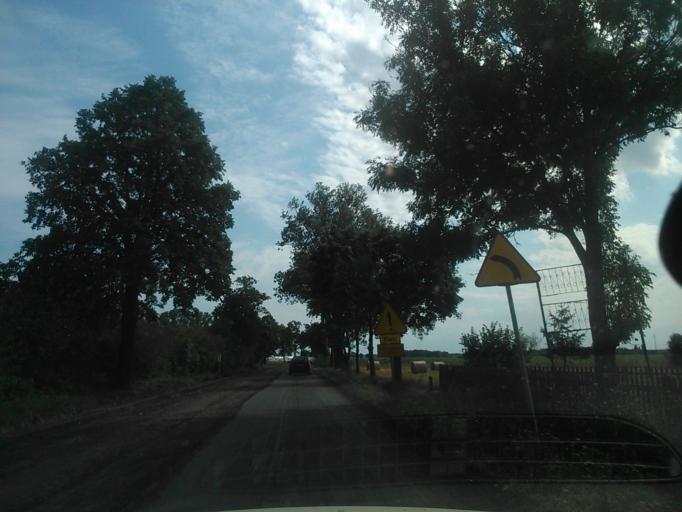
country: PL
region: Warmian-Masurian Voivodeship
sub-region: Powiat dzialdowski
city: Ilowo -Osada
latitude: 53.1974
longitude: 20.2516
